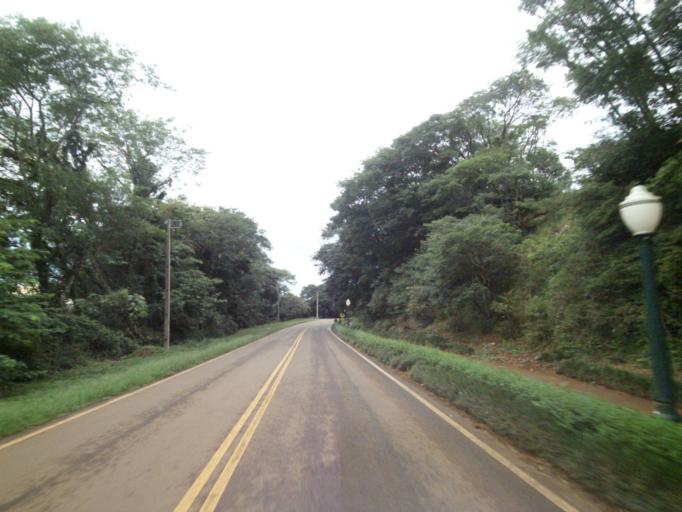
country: BR
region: Parana
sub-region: Guaraniacu
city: Guaraniacu
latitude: -25.0985
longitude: -52.8868
